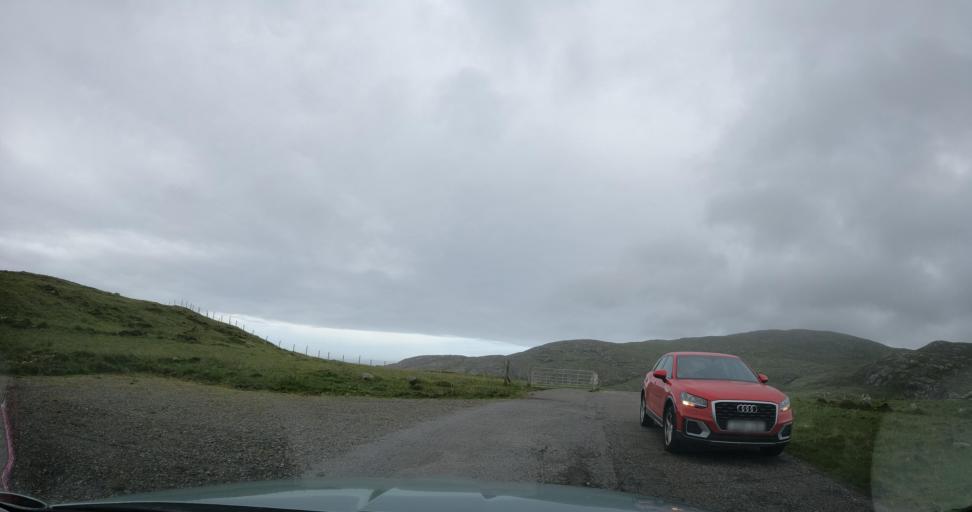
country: GB
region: Scotland
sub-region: Eilean Siar
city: Barra
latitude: 56.9419
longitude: -7.5440
